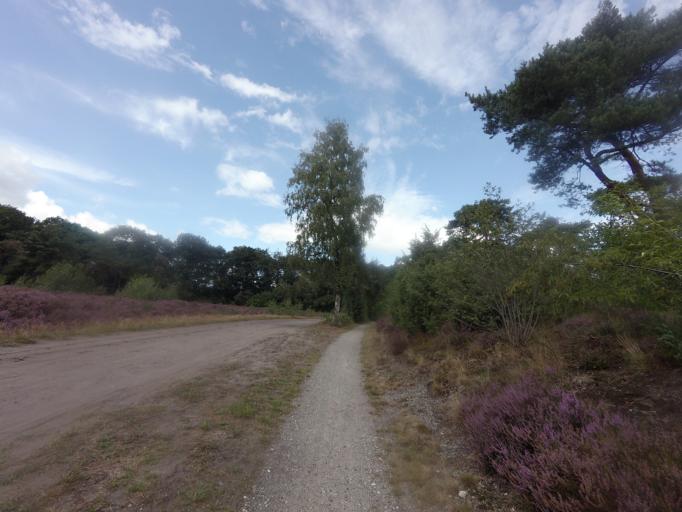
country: NL
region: Overijssel
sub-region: Gemeente Staphorst
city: Staphorst
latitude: 52.6516
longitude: 6.2626
